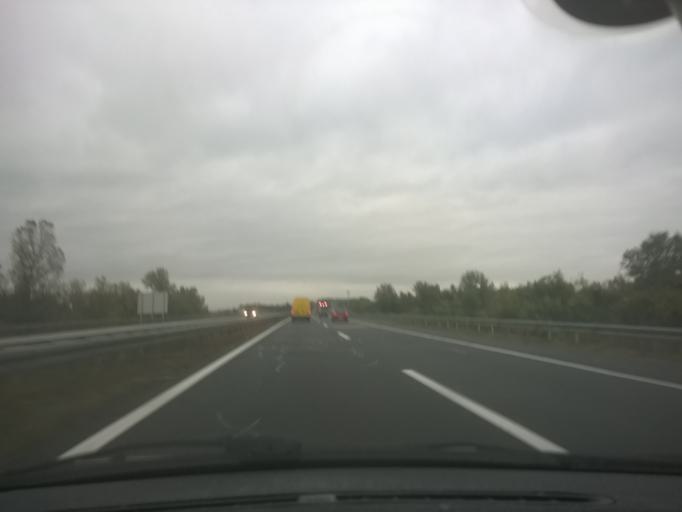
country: HR
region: Grad Zagreb
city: Jezdovec
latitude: 45.7993
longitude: 15.8417
